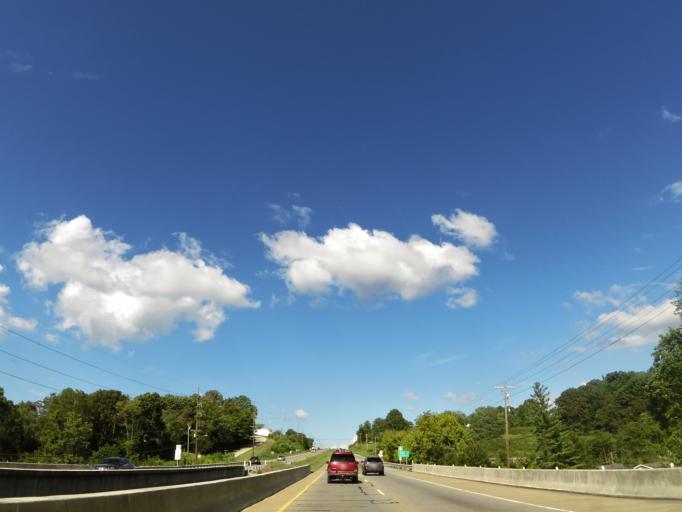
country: US
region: Tennessee
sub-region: Greene County
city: Greeneville
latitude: 36.1758
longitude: -82.8304
